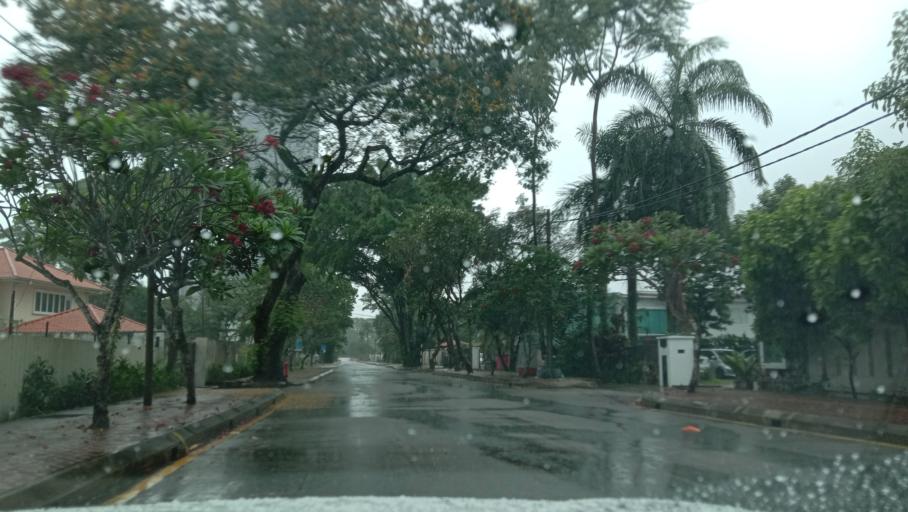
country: MY
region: Kuala Lumpur
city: Kuala Lumpur
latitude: 3.1706
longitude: 101.7163
